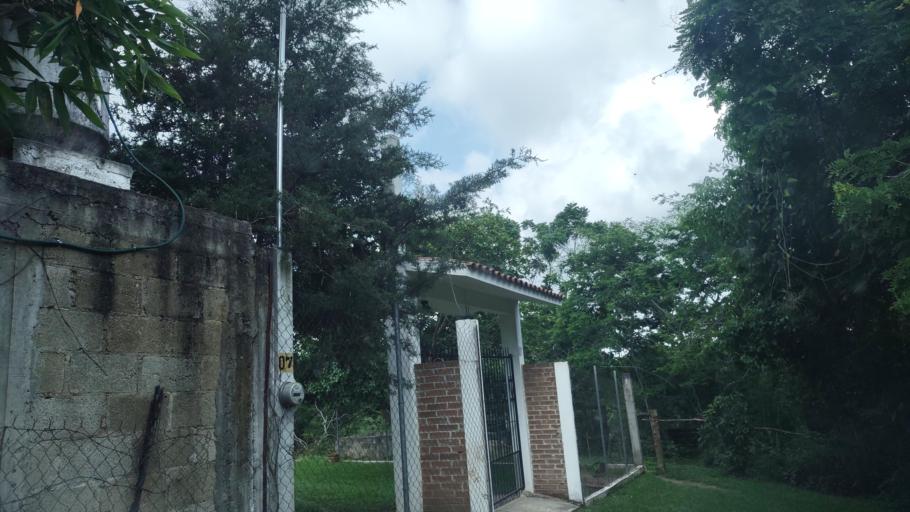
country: MX
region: Veracruz
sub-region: Emiliano Zapata
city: Jacarandas
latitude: 19.4692
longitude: -96.8339
